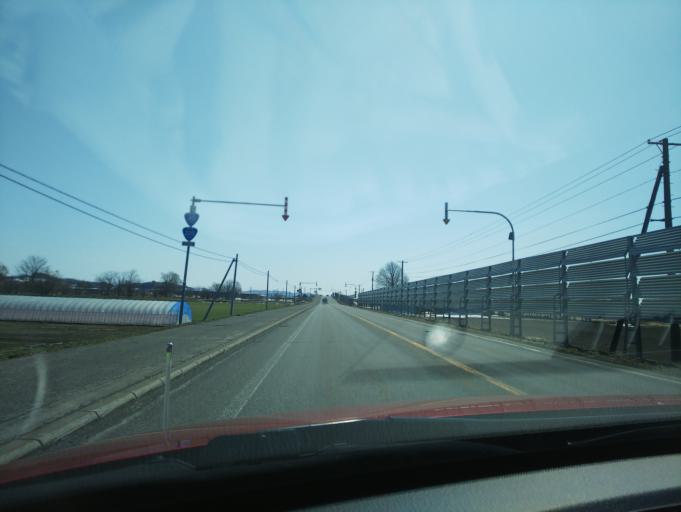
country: JP
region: Hokkaido
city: Nayoro
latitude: 44.1996
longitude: 142.3950
